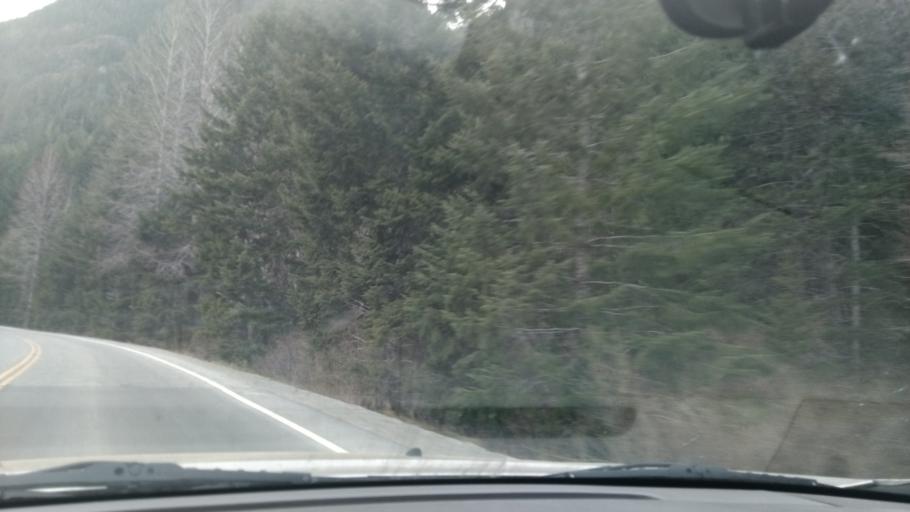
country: CA
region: British Columbia
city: Campbell River
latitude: 49.8543
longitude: -125.8364
